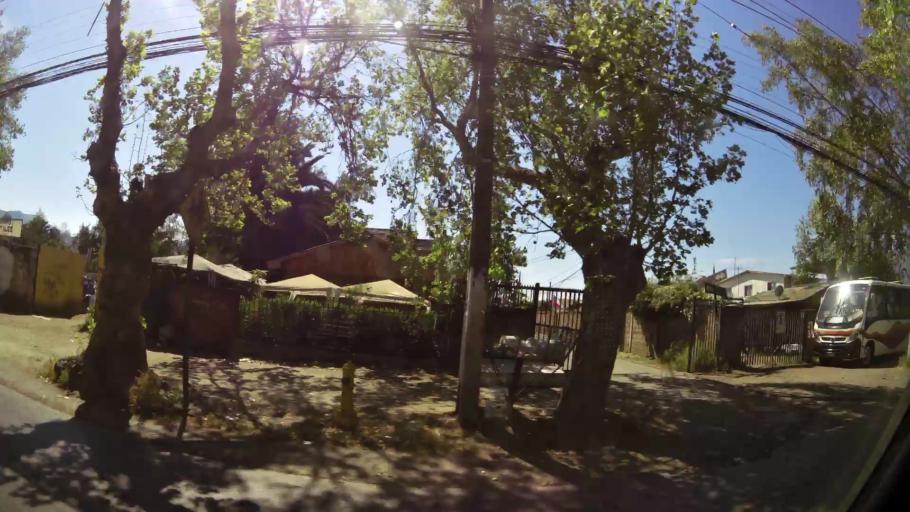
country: CL
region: Santiago Metropolitan
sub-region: Provincia de Talagante
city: Penaflor
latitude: -33.6115
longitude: -70.8930
